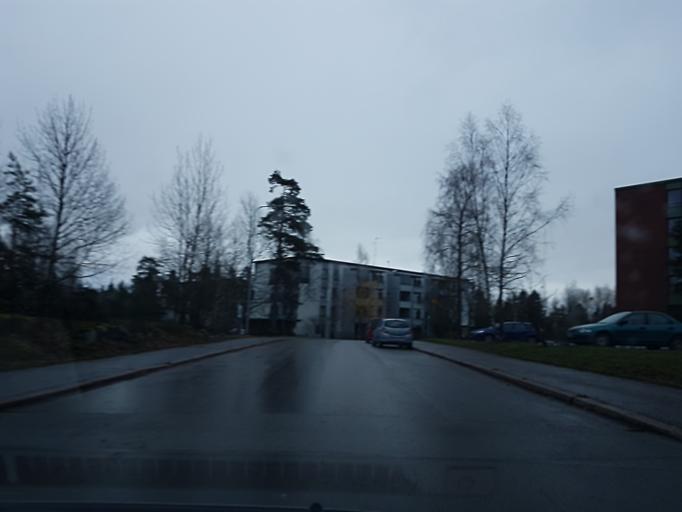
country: FI
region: Uusimaa
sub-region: Helsinki
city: Vantaa
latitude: 60.2383
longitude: 25.1229
